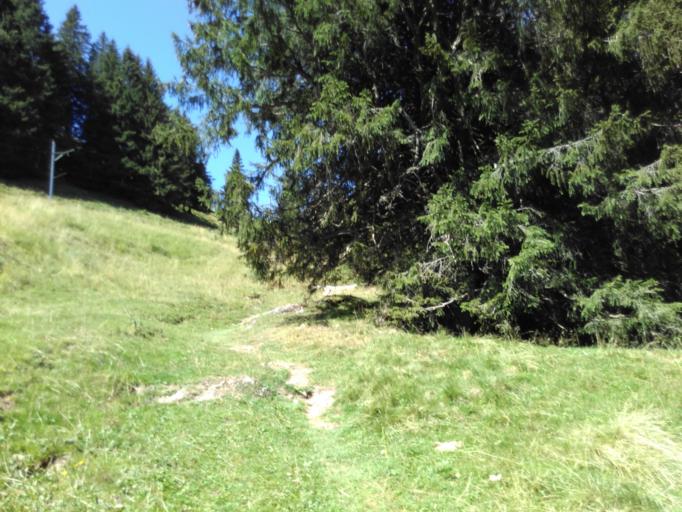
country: CH
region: Lucerne
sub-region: Lucerne-Land District
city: Vitznau
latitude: 47.0491
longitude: 8.4735
